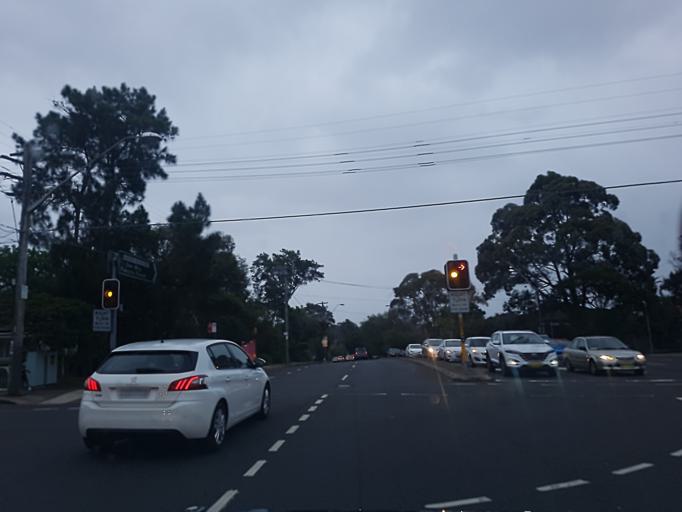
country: AU
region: New South Wales
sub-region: Willoughby
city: Castlecrag
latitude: -33.8024
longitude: 151.2115
